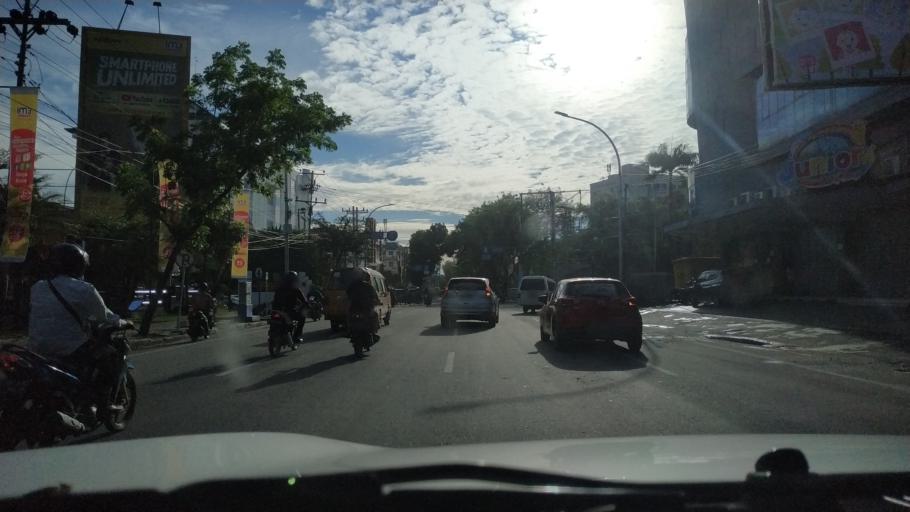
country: ID
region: North Sumatra
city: Medan
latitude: 3.5988
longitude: 98.6864
